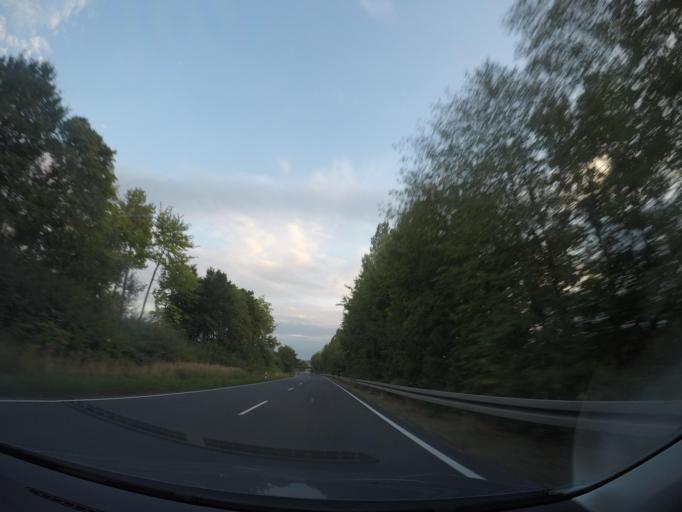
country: DE
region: Lower Saxony
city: Seesen
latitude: 51.8797
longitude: 10.1714
